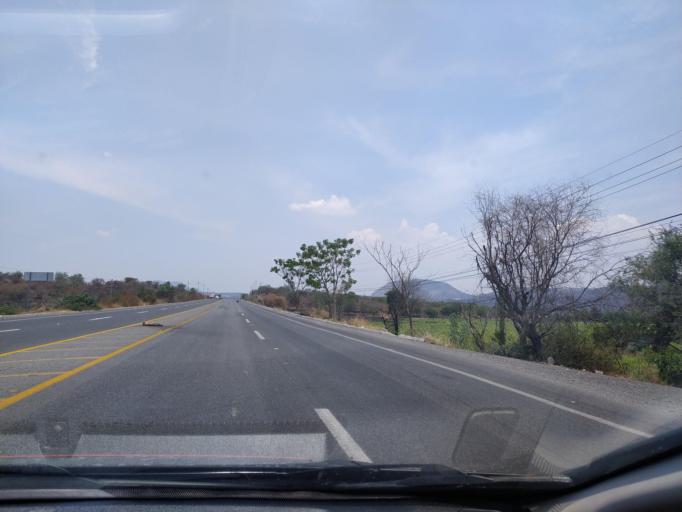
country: MX
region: Jalisco
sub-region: Acatlan de Juarez
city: Villa de los Ninos
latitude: 20.4028
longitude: -103.5939
